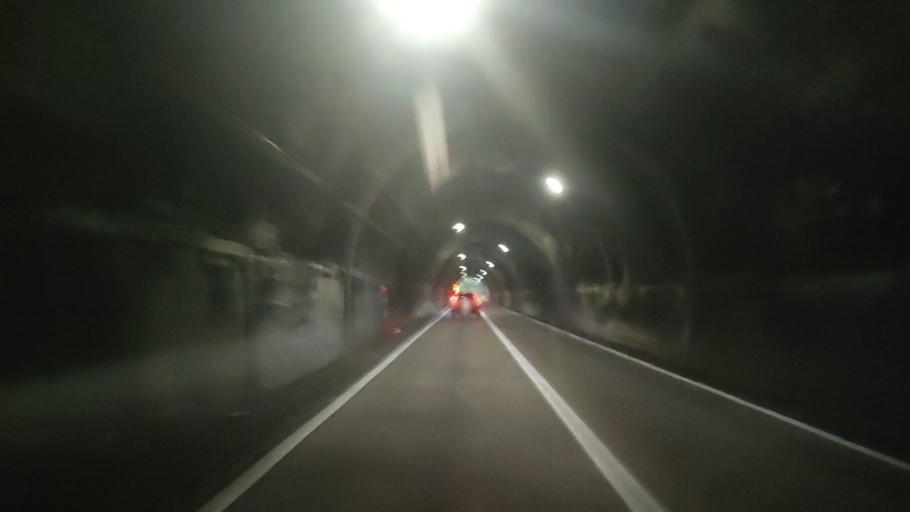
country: JP
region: Mie
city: Ise
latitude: 34.4139
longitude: 136.7633
